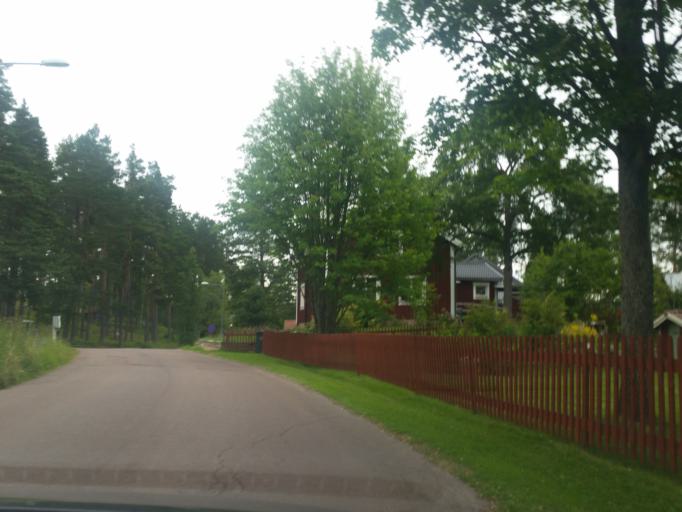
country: SE
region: Dalarna
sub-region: Leksand Municipality
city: Smedby
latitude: 60.6750
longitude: 15.1046
